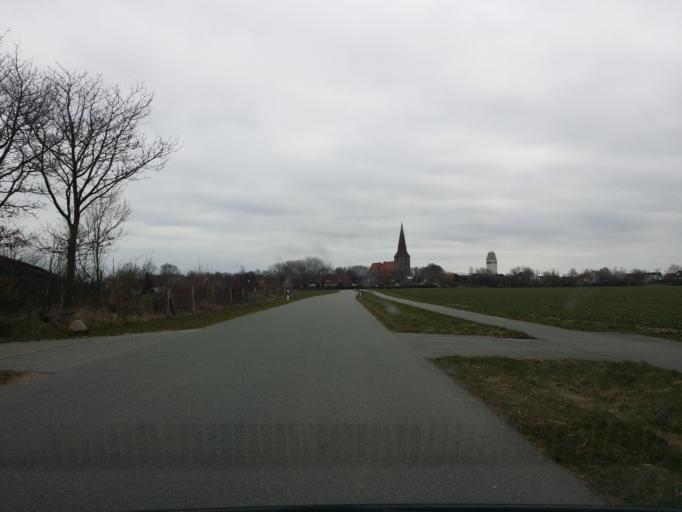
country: DE
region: Schleswig-Holstein
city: Grossenbrode
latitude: 54.4823
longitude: 11.0596
